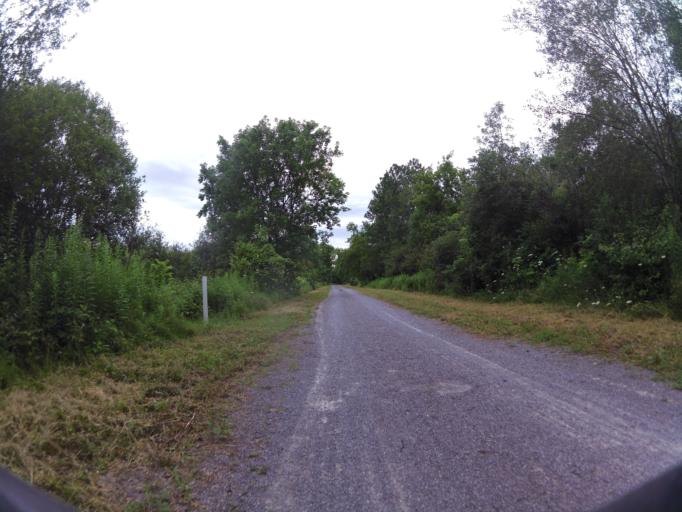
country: CA
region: Ontario
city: Ottawa
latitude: 45.2640
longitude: -75.6232
